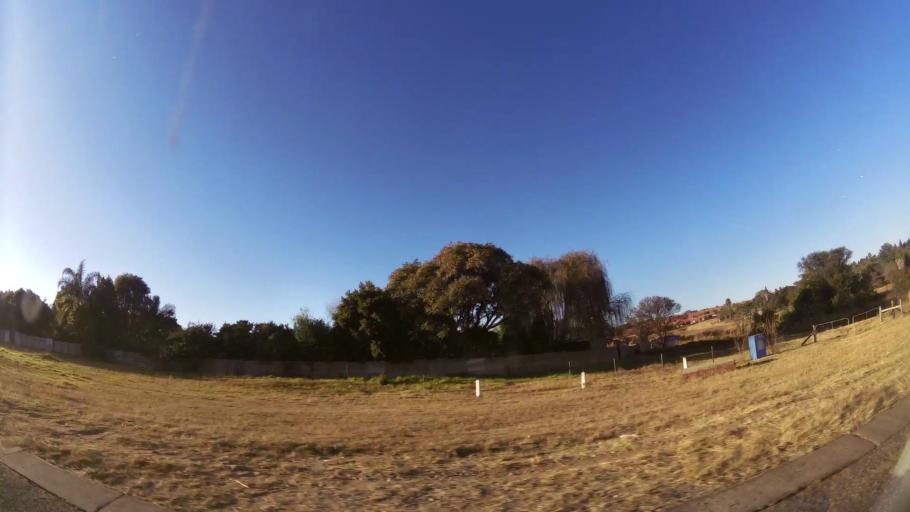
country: ZA
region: Gauteng
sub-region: City of Tshwane Metropolitan Municipality
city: Centurion
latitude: -25.8968
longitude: 28.1461
